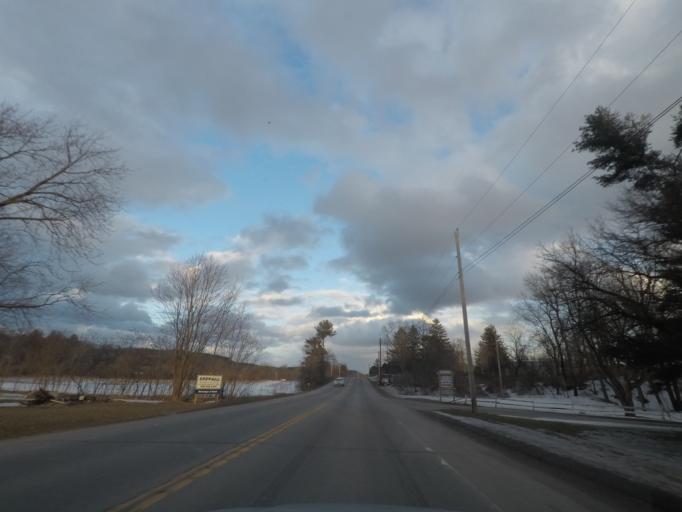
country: US
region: New York
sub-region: Montgomery County
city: Saint Johnsville
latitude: 43.0037
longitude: -74.7130
